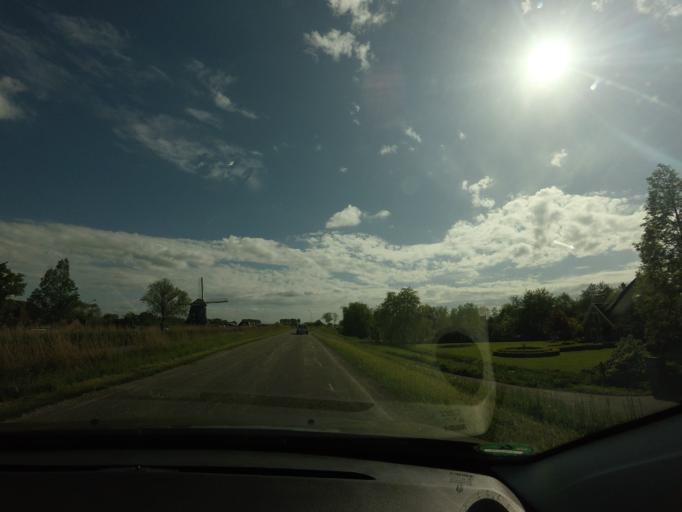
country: NL
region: North Holland
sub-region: Gemeente Heerhugowaard
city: Heerhugowaard
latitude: 52.6620
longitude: 4.8672
